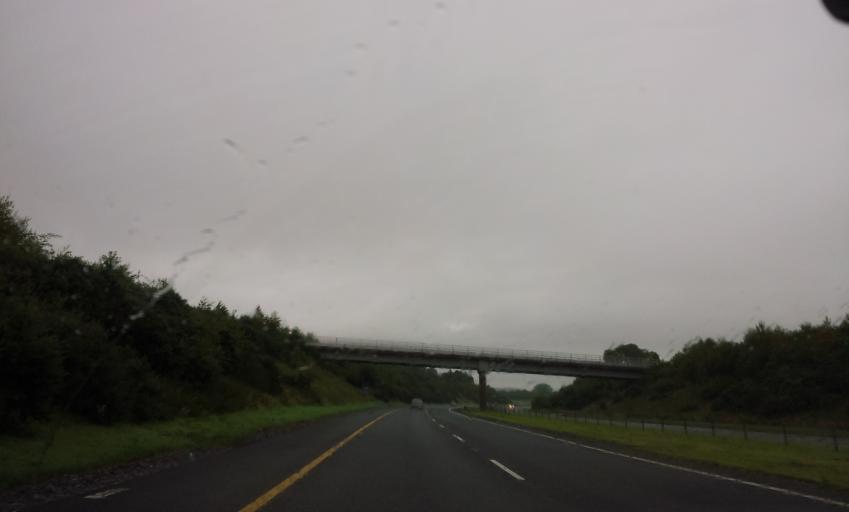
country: IE
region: Munster
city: Cahir
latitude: 52.3774
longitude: -7.9528
